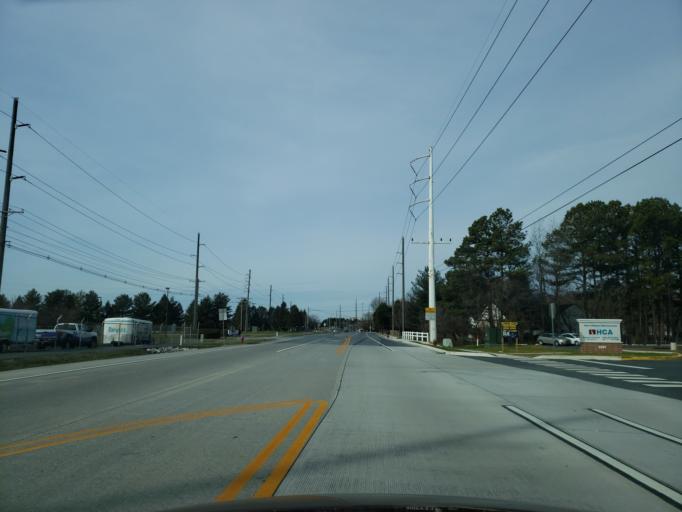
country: US
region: Delaware
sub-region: Kent County
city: Rodney Village
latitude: 39.1510
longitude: -75.5527
